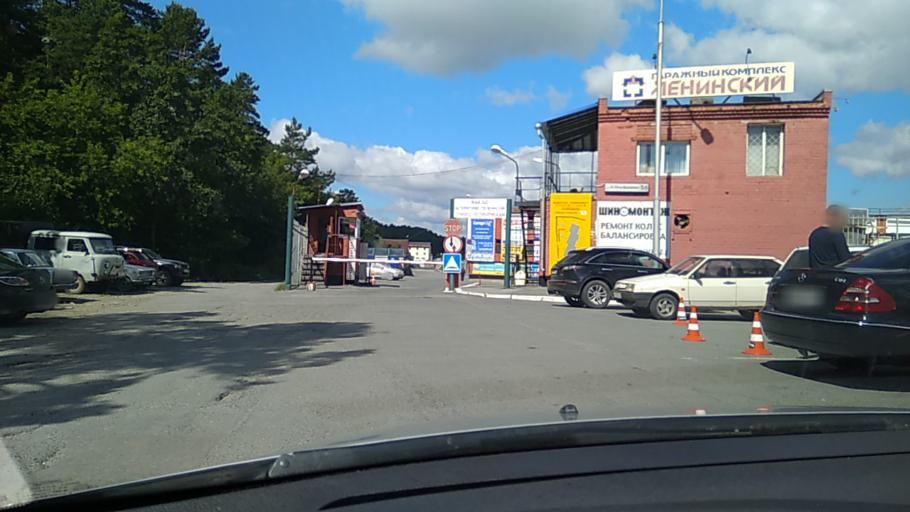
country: RU
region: Sverdlovsk
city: Sovkhoznyy
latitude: 56.7918
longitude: 60.5694
